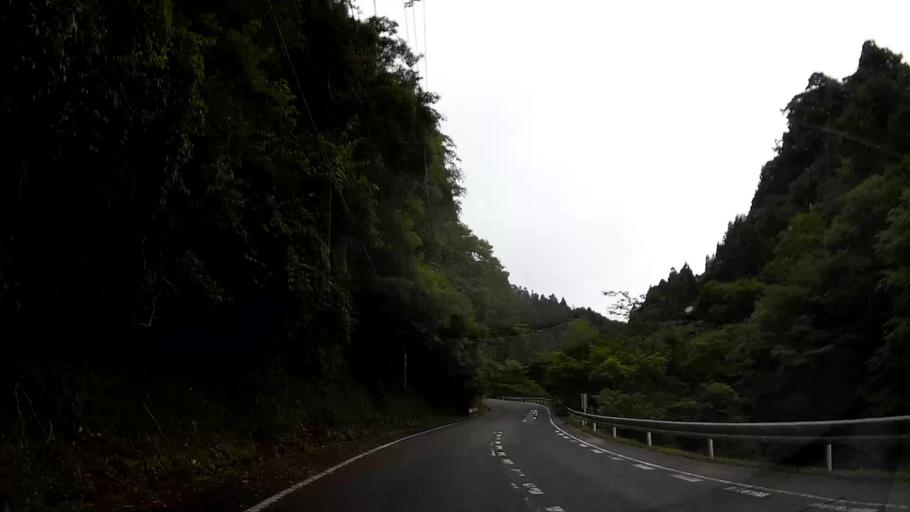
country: JP
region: Kumamoto
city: Kikuchi
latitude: 33.0733
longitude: 130.9291
